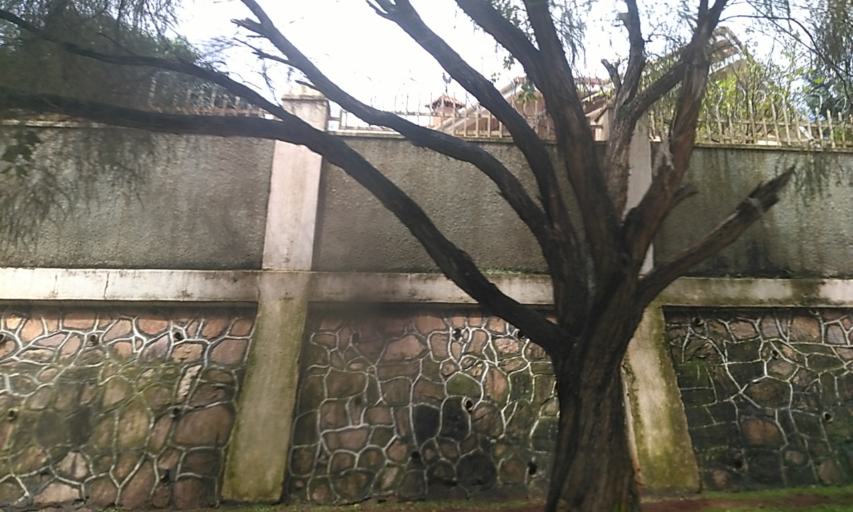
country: UG
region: Central Region
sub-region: Kampala District
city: Kampala
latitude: 0.3292
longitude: 32.6004
